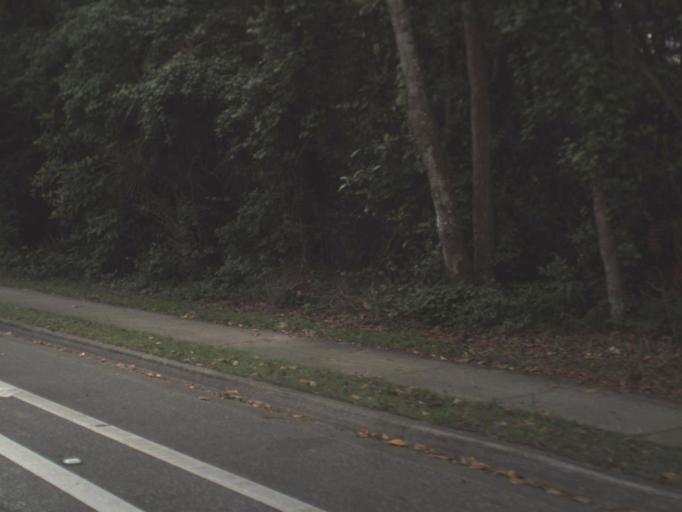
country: US
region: Florida
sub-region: Clay County
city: Orange Park
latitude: 30.1654
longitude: -81.7157
